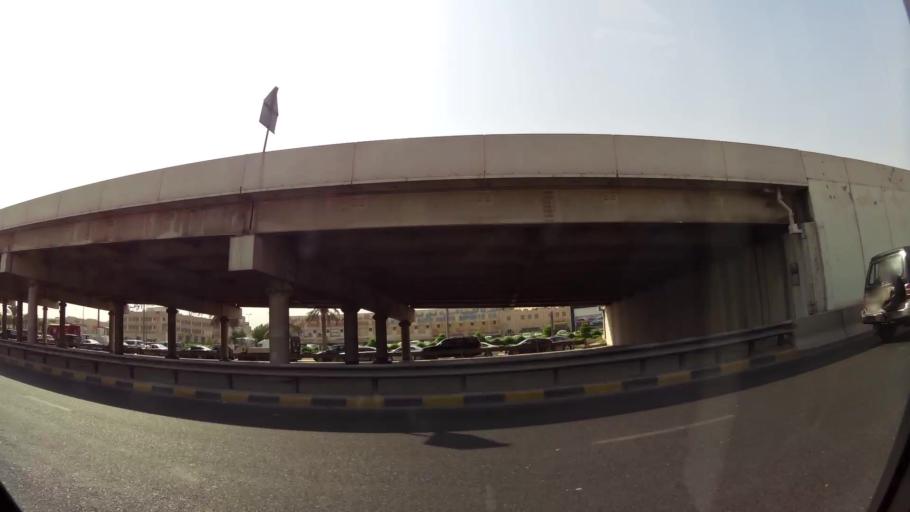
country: KW
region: Al Asimah
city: Ash Shamiyah
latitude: 29.3343
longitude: 47.9516
